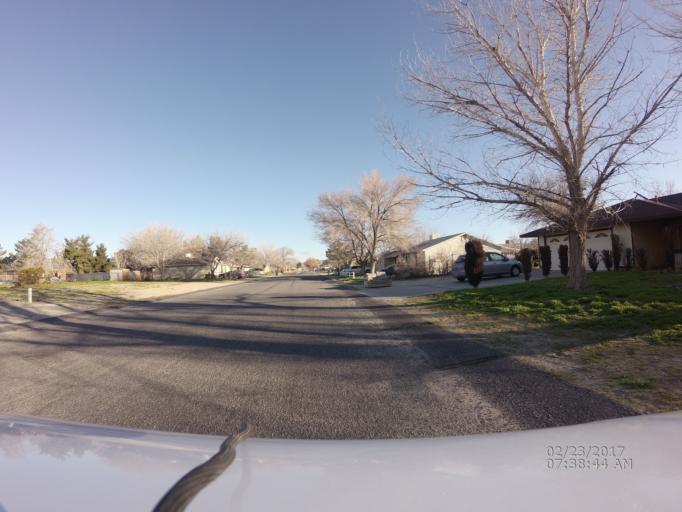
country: US
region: California
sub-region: Los Angeles County
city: Lake Los Angeles
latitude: 34.6147
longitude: -117.8105
